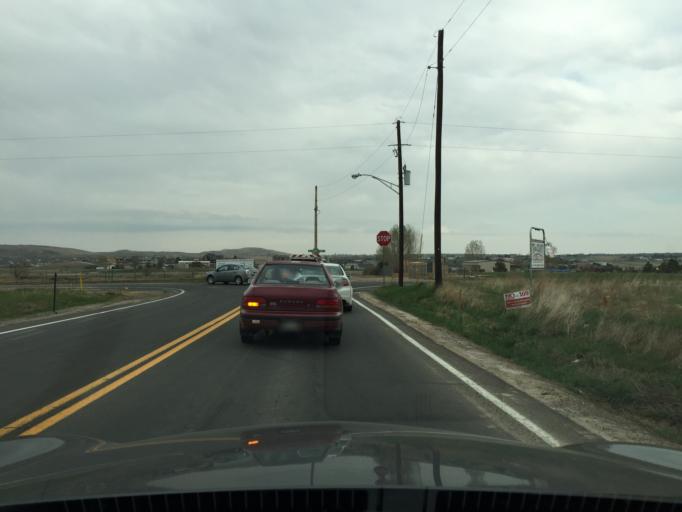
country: US
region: Colorado
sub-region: Boulder County
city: Erie
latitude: 40.0148
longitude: -105.0560
